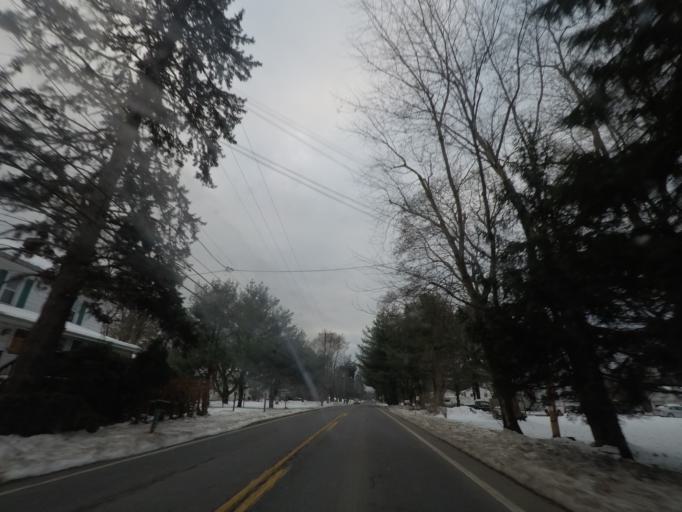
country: US
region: New York
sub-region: Ulster County
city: Clintondale
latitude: 41.6718
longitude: -74.1044
